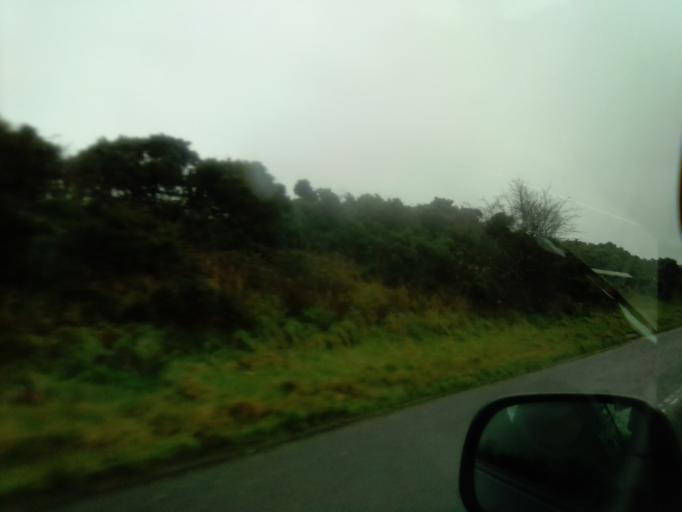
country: GB
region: Northern Ireland
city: Newtownstewart
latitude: 54.7377
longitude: -7.4344
